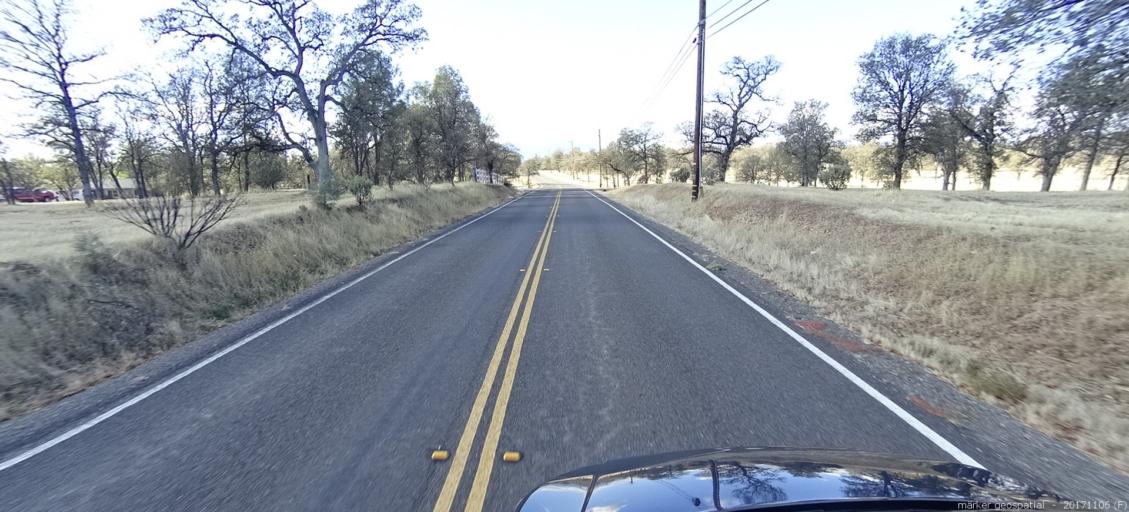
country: US
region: California
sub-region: Shasta County
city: Palo Cedro
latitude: 40.5929
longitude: -122.2643
